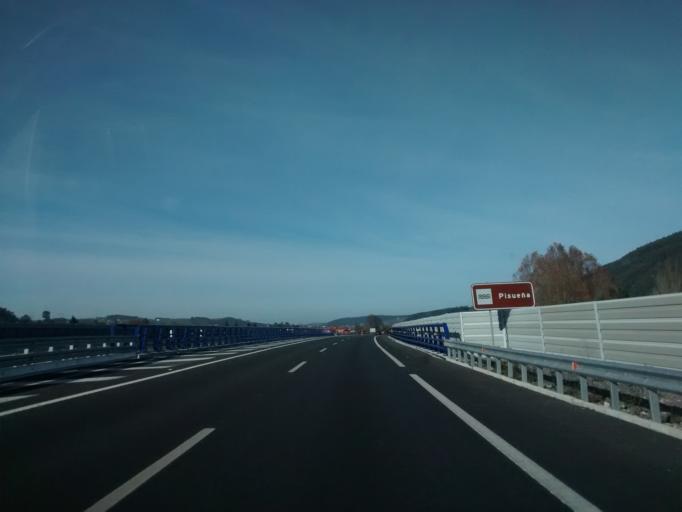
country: ES
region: Cantabria
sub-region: Provincia de Cantabria
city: Puente Viesgo
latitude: 43.3129
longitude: -3.9455
